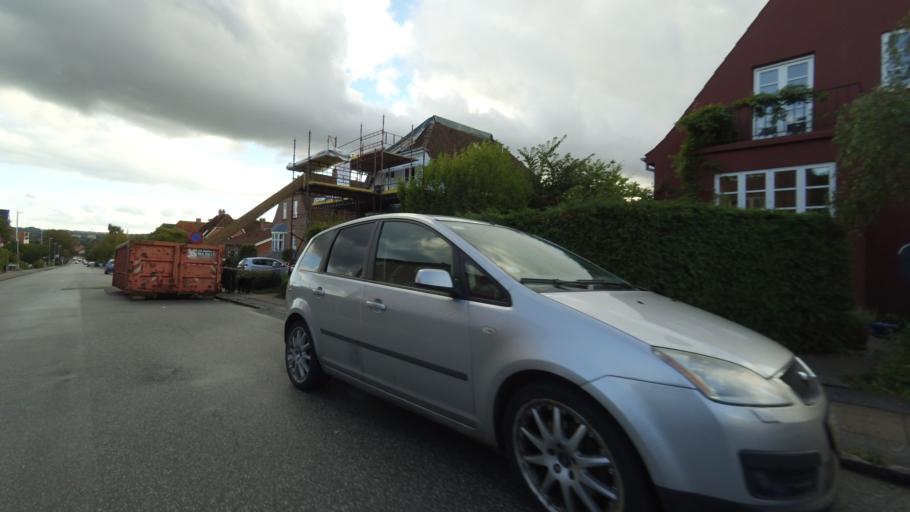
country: DK
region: Central Jutland
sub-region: Arhus Kommune
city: Stavtrup
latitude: 56.1534
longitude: 10.1548
